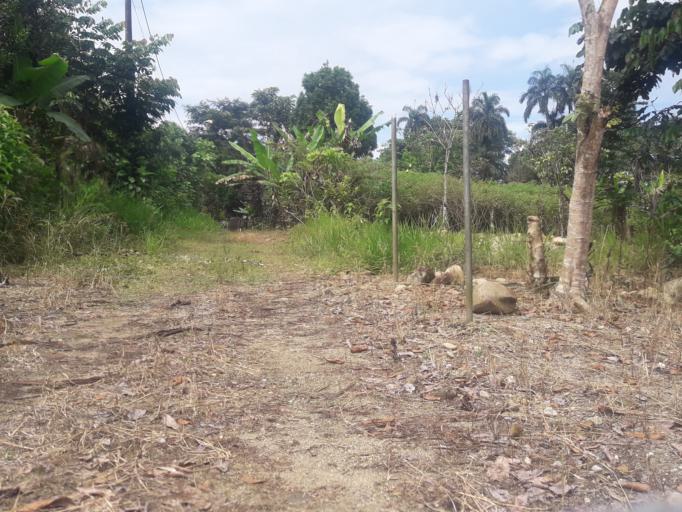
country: EC
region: Napo
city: Tena
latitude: -0.9784
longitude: -77.8479
